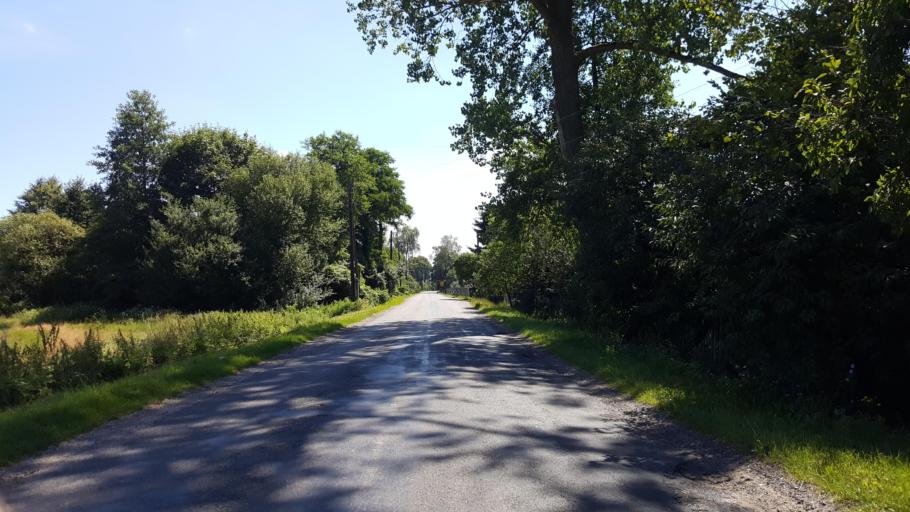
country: BY
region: Brest
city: Charnawchytsy
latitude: 52.3272
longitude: 23.6085
